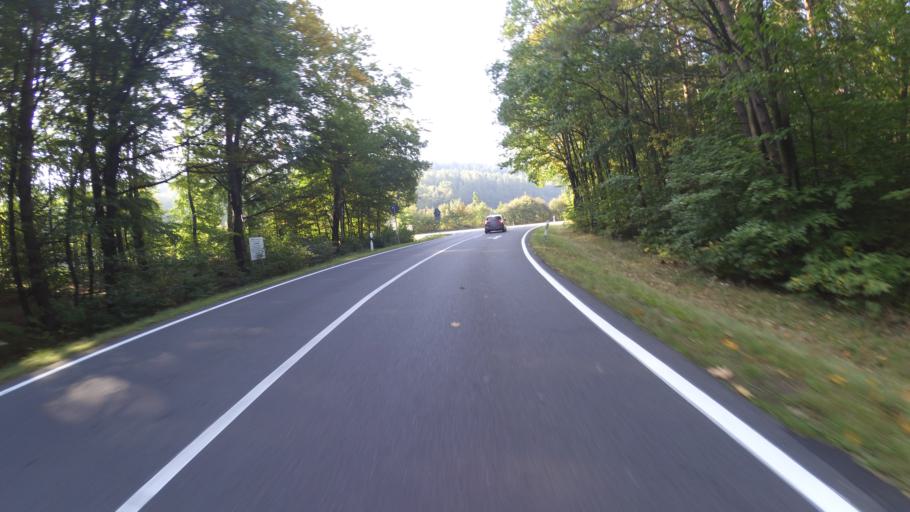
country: DE
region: Rheinland-Pfalz
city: Mittelbrunn
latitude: 49.3969
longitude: 7.5393
